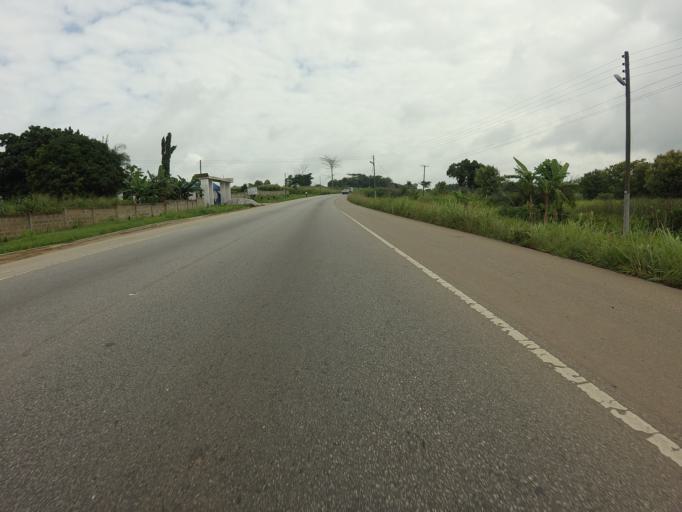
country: GH
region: Ashanti
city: Tafo
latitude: 6.9730
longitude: -1.6850
